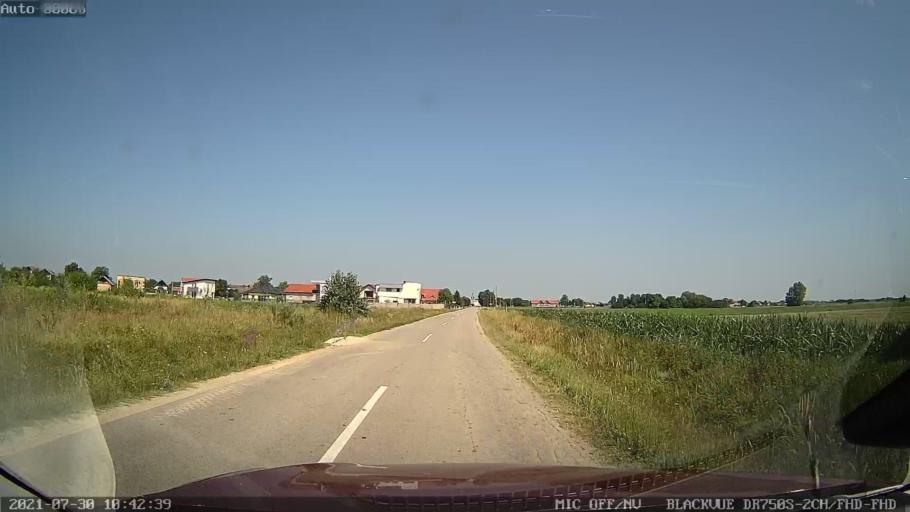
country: HR
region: Medimurska
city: Kursanec
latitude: 46.2867
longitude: 16.4085
